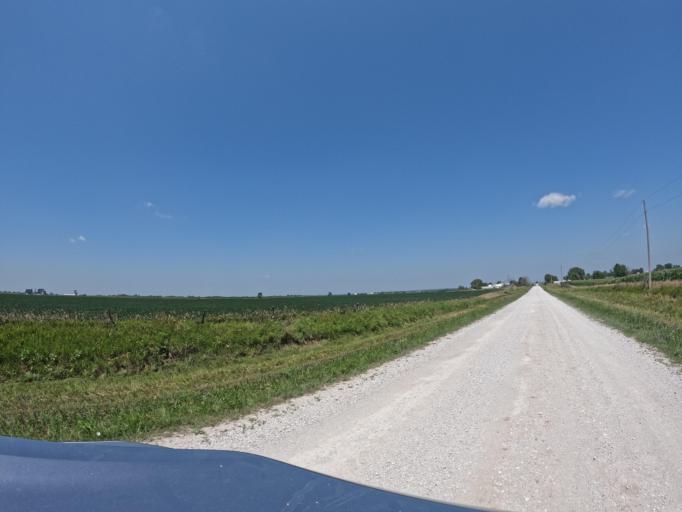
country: US
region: Iowa
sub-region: Keokuk County
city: Sigourney
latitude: 41.2659
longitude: -92.1700
